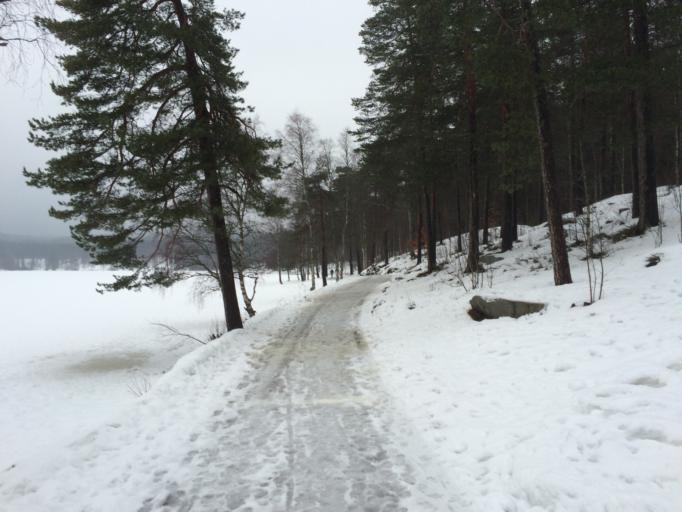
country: NO
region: Oslo
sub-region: Oslo
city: Oslo
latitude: 59.9718
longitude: 10.7314
